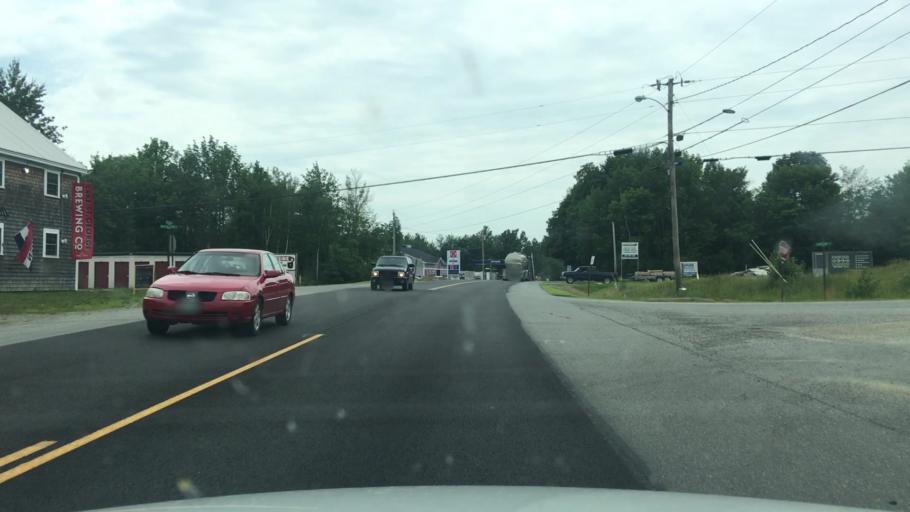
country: US
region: Maine
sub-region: Knox County
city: Washington
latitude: 44.3871
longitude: -69.3583
